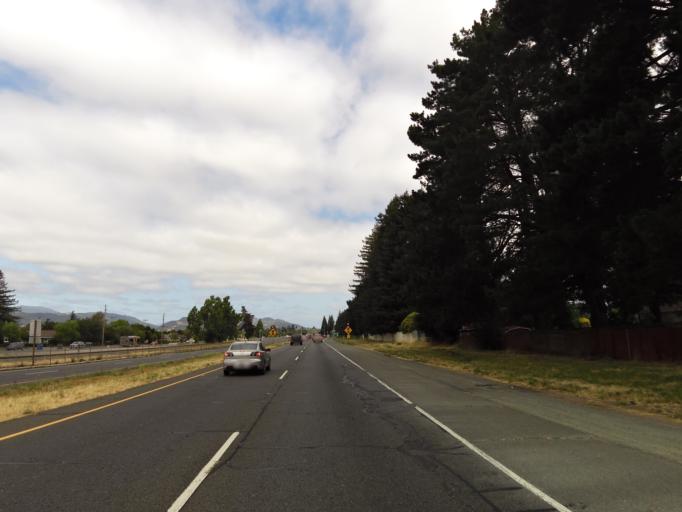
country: US
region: California
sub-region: Napa County
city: Napa
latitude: 38.3280
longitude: -122.3148
